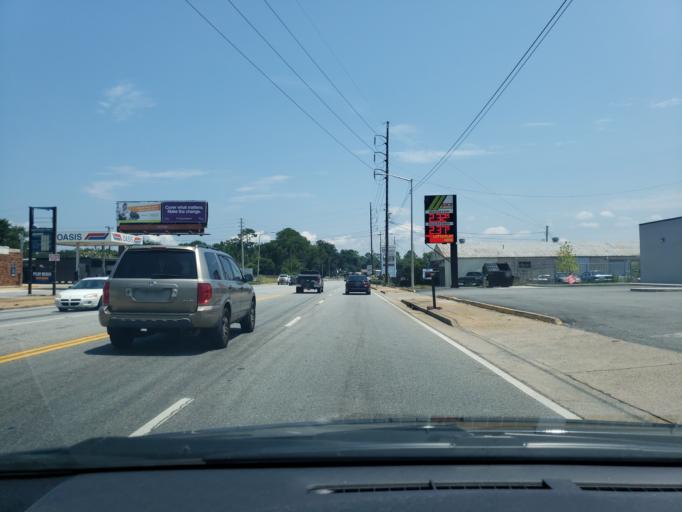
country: US
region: Georgia
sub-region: Dougherty County
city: Albany
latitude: 31.5812
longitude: -84.1904
